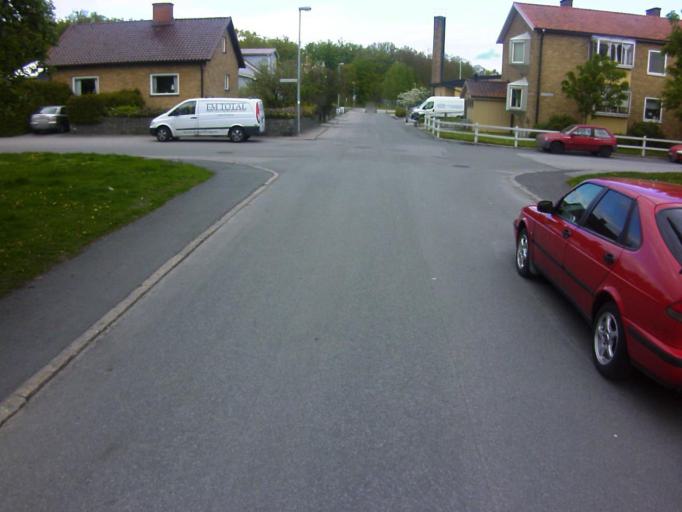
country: SE
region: Blekinge
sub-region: Solvesborgs Kommun
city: Soelvesborg
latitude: 56.0574
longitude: 14.5860
